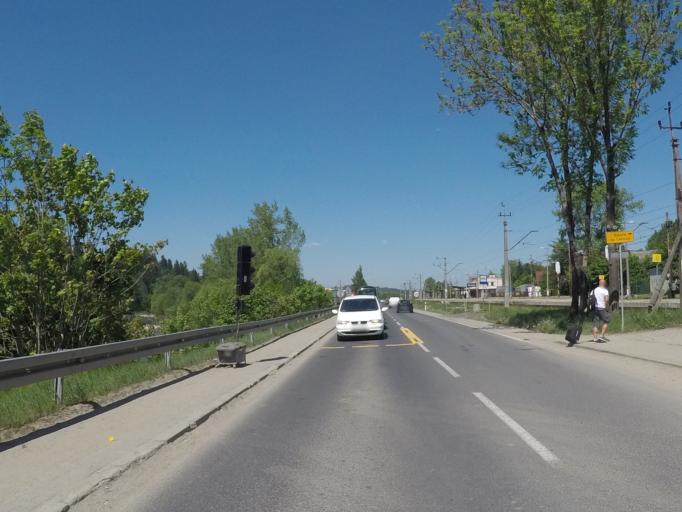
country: PL
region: Lesser Poland Voivodeship
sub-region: Powiat tatrzanski
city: Poronin
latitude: 49.3416
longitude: 20.0032
